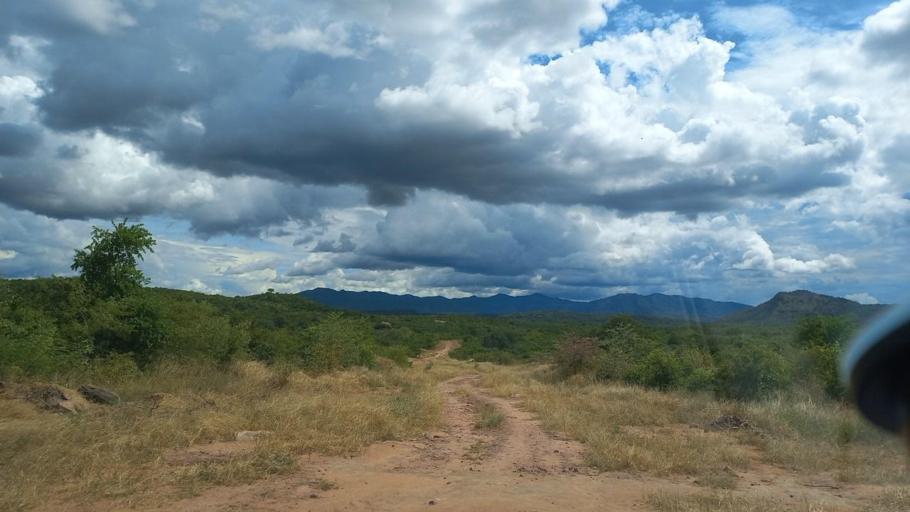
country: ZM
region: Lusaka
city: Luangwa
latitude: -15.6265
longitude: 30.3923
